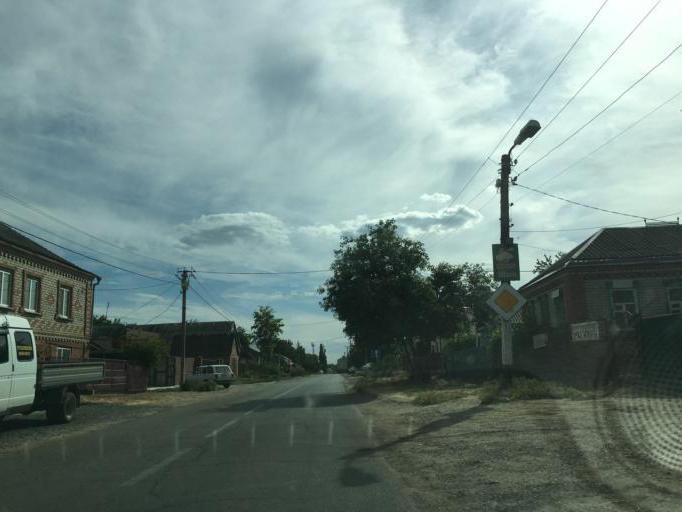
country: RU
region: Krasnodarskiy
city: Kushchevskaya
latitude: 46.5590
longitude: 39.6328
